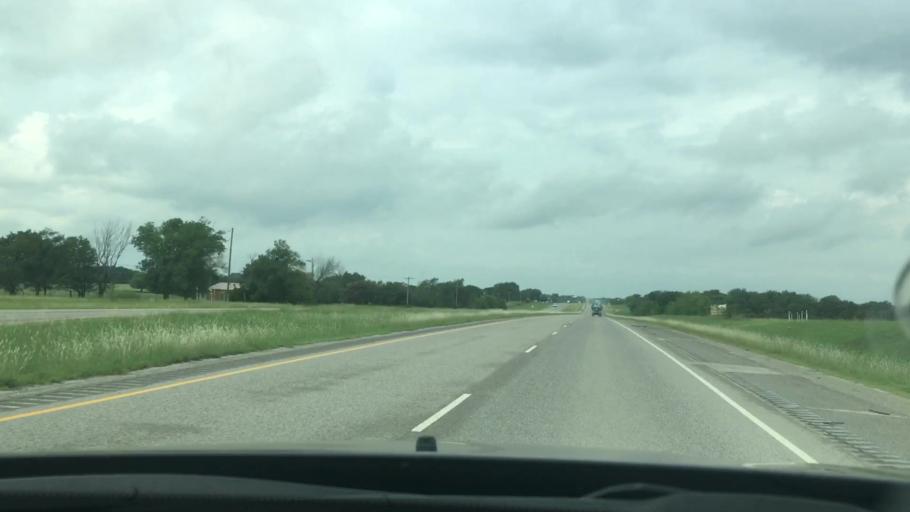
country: US
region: Oklahoma
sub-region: Carter County
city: Wilson
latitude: 34.1731
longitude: -97.4636
